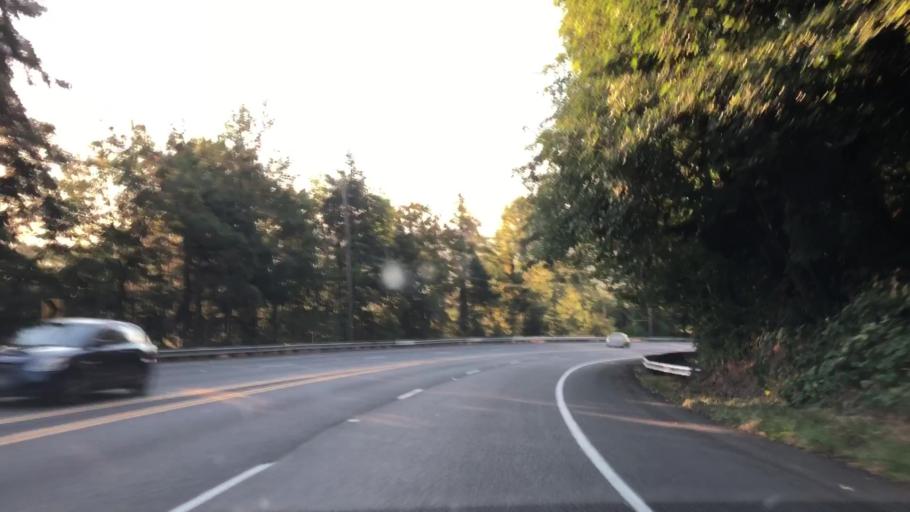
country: US
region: Washington
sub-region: King County
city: Lakeland North
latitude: 47.3578
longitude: -122.2707
